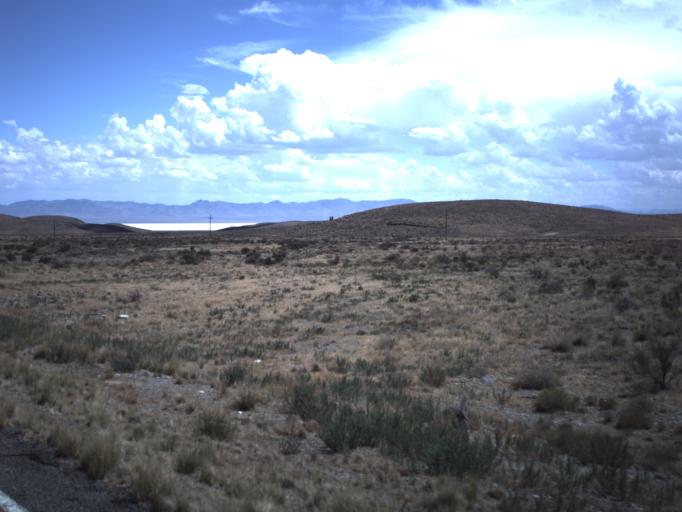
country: US
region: Utah
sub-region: Beaver County
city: Milford
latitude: 39.0376
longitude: -113.3219
